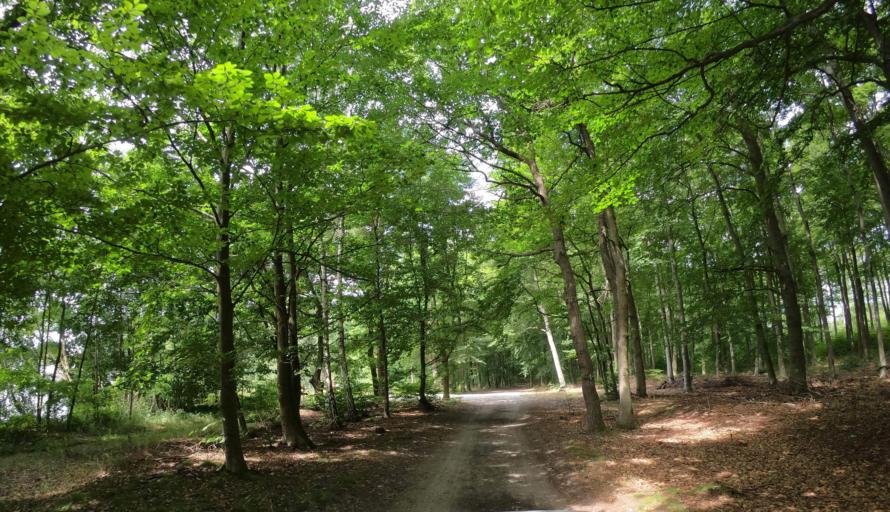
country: PL
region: West Pomeranian Voivodeship
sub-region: Powiat gryfinski
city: Stare Czarnowo
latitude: 53.3389
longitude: 14.7958
